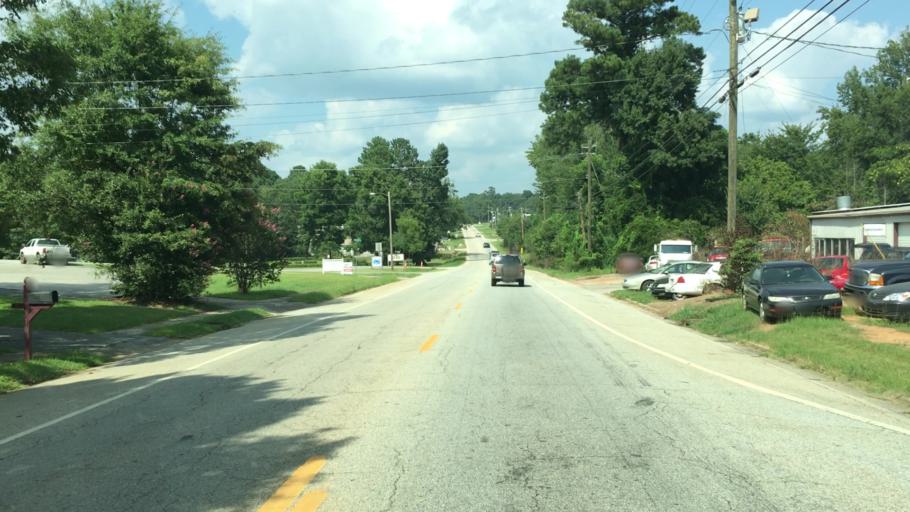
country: US
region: Georgia
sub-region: Monroe County
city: Forsyth
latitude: 33.0478
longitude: -83.9332
